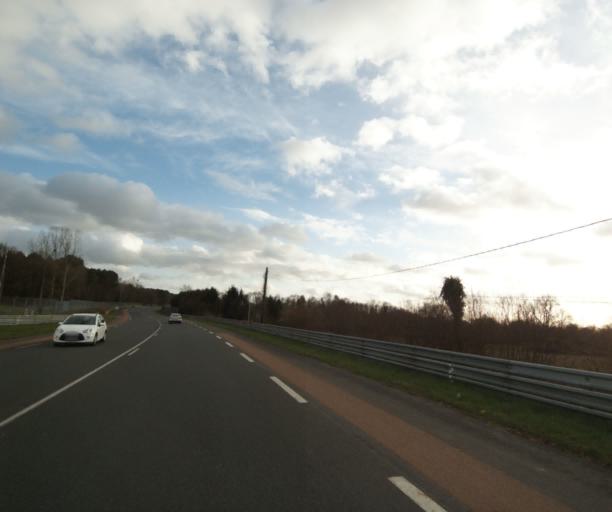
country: FR
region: Pays de la Loire
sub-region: Departement de la Sarthe
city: Arnage
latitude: 47.9320
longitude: 0.2092
